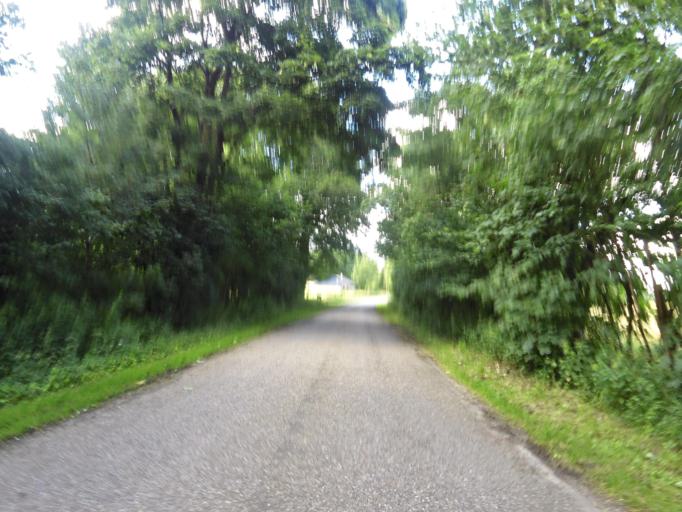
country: DK
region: South Denmark
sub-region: Tonder Kommune
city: Toftlund
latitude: 55.1472
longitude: 9.0851
